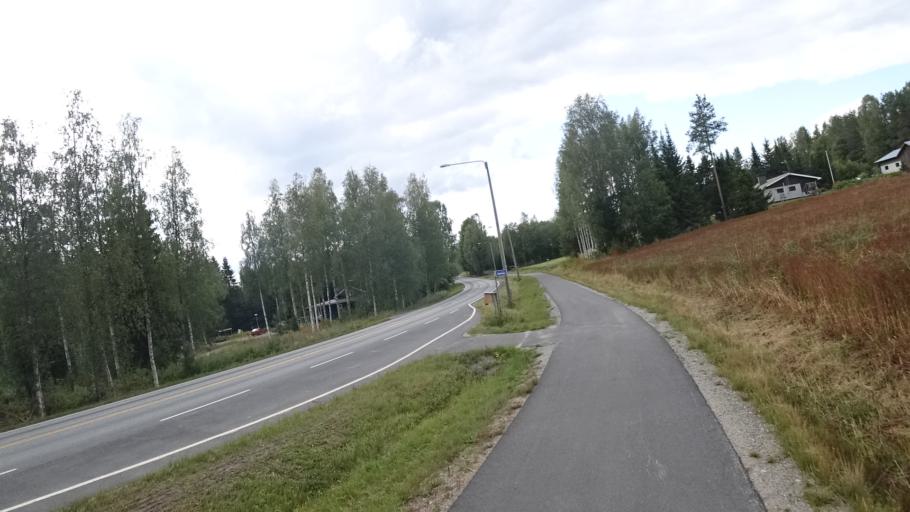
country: FI
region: North Karelia
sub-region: Joensuu
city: Ilomantsi
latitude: 62.6528
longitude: 30.9679
